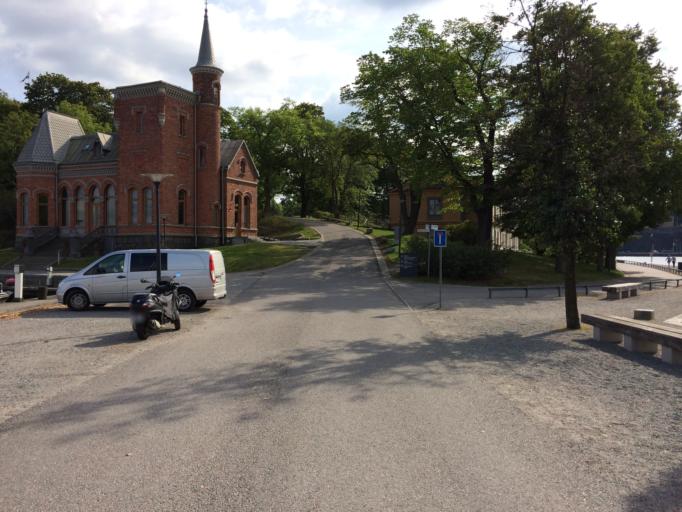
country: SE
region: Stockholm
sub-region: Stockholms Kommun
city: OEstermalm
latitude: 59.3235
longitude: 18.0878
